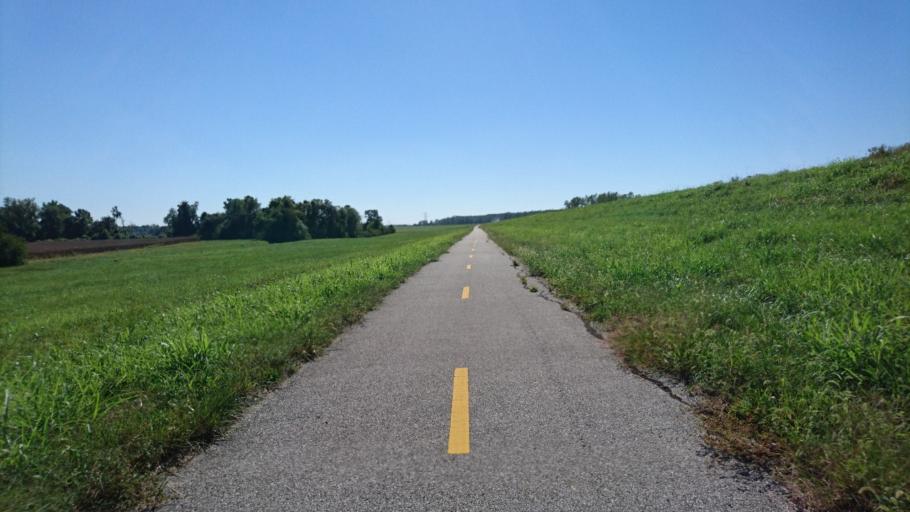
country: US
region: Illinois
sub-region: Madison County
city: Hartford
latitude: 38.7963
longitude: -90.1120
